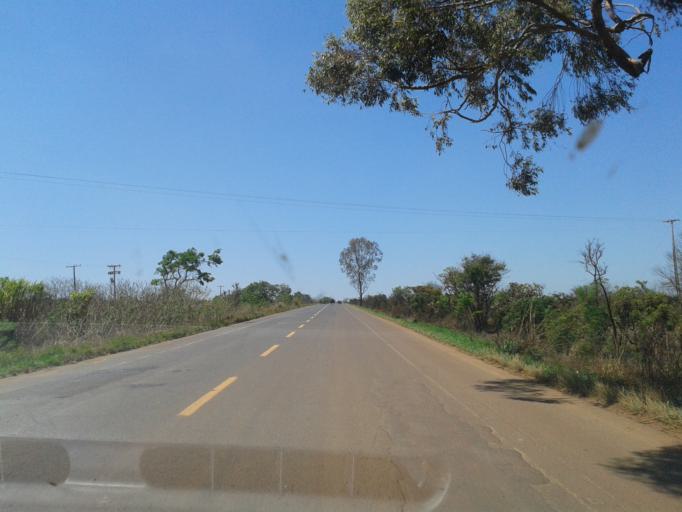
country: BR
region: Minas Gerais
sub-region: Araxa
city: Araxa
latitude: -19.4126
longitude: -47.3037
